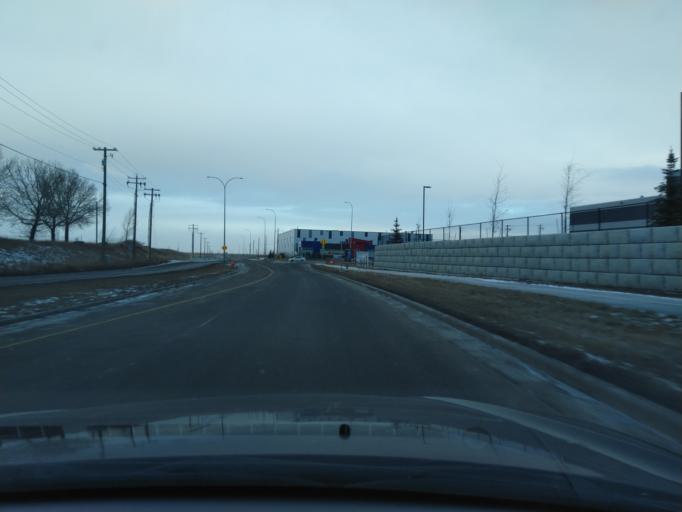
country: CA
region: Alberta
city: Calgary
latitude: 51.1603
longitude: -114.0250
